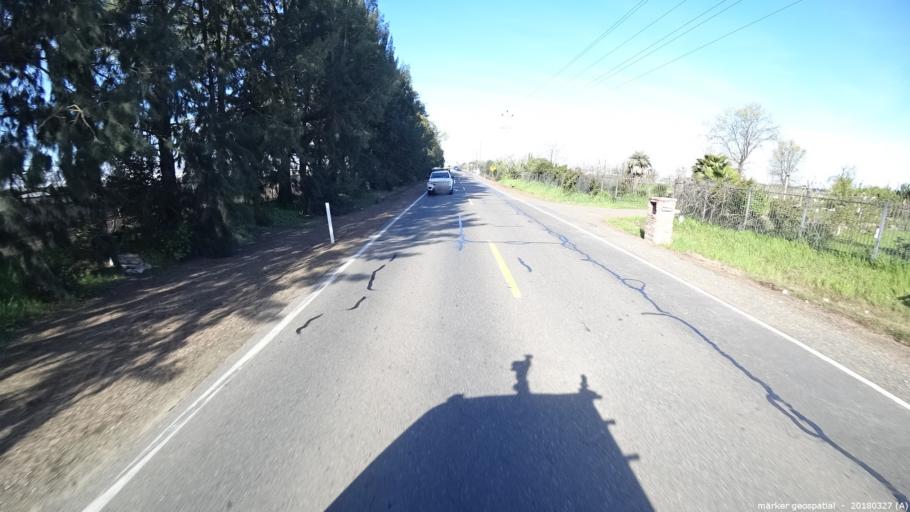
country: US
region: California
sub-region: Sacramento County
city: Vineyard
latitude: 38.5108
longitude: -121.3319
